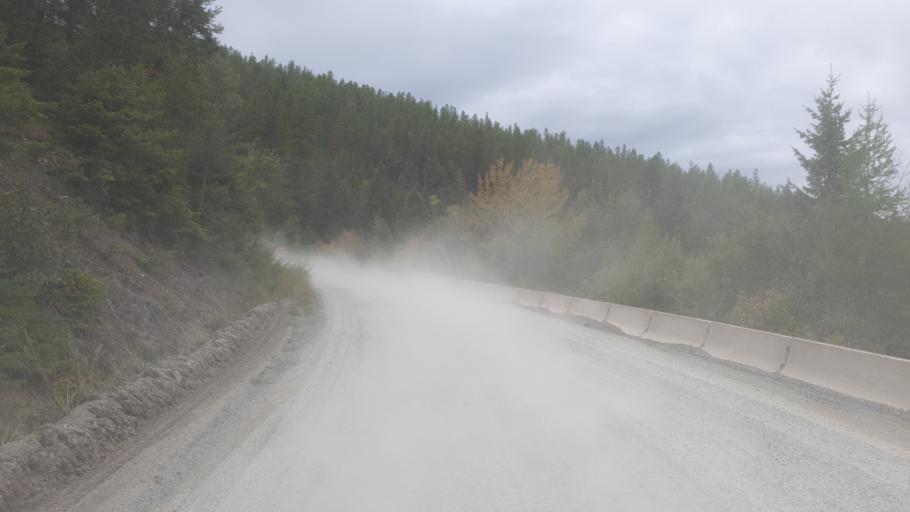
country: US
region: Montana
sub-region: Flathead County
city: Lakeside
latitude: 47.9897
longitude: -114.3169
